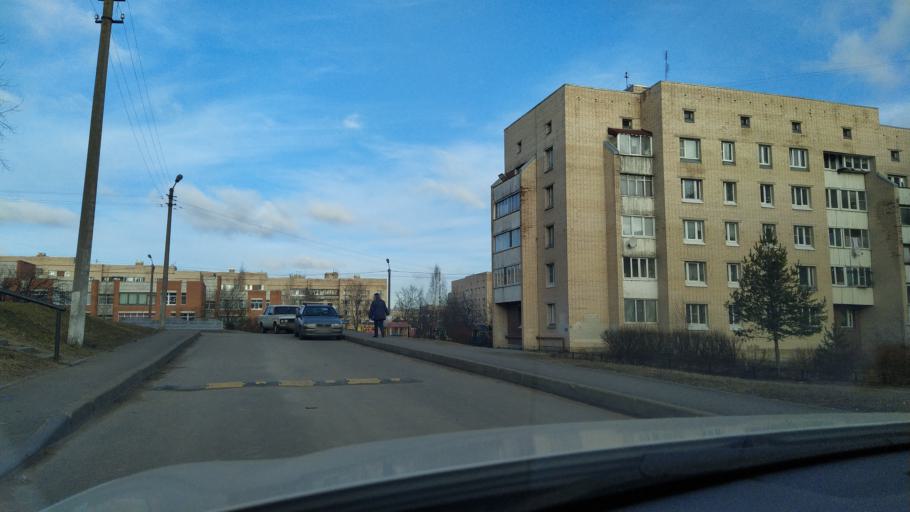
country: RU
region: St.-Petersburg
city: Pushkin
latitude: 59.7357
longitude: 30.4034
